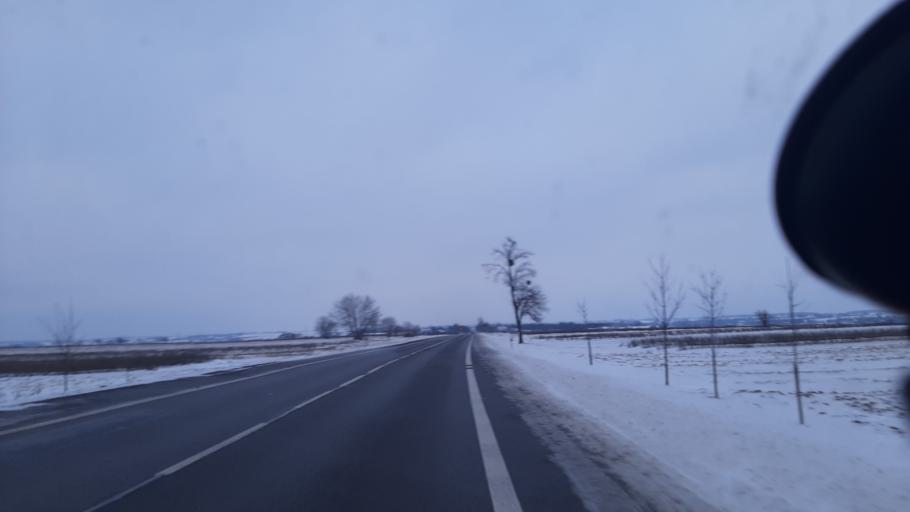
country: PL
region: Lublin Voivodeship
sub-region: Powiat pulawski
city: Markuszow
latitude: 51.3808
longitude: 22.2339
